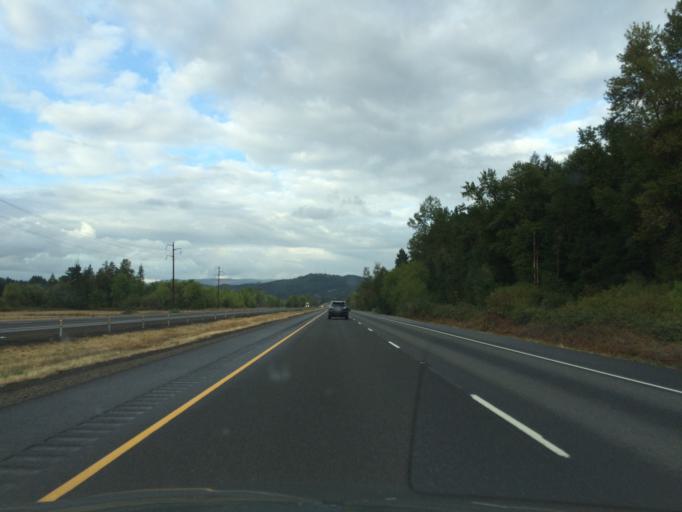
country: US
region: Oregon
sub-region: Lane County
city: Cottage Grove
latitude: 43.7573
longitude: -123.0939
